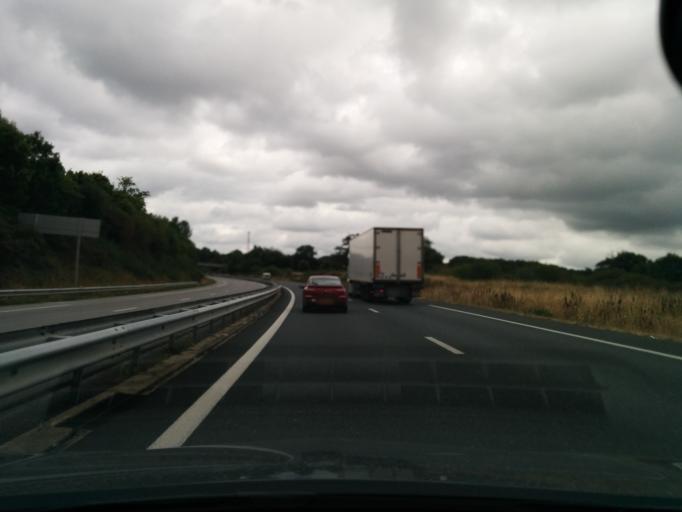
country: FR
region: Limousin
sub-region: Departement de la Haute-Vienne
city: Bessines-sur-Gartempe
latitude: 46.1257
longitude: 1.3806
